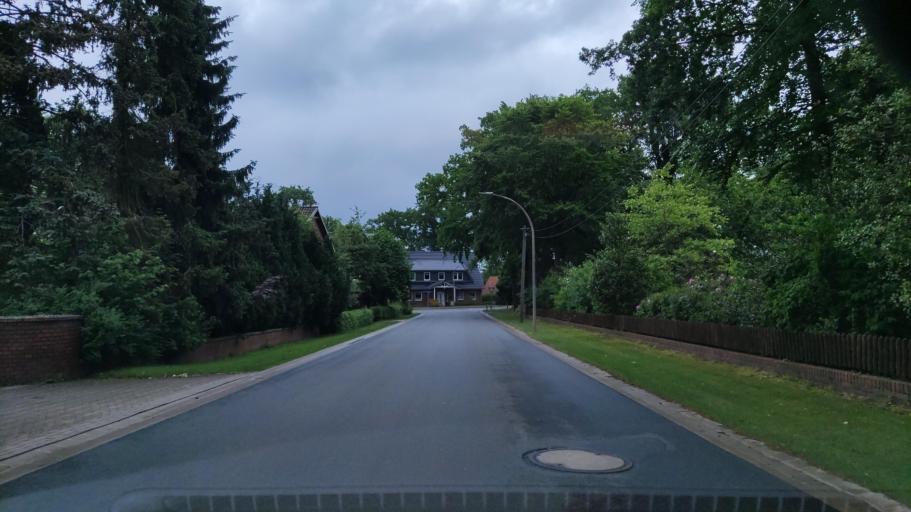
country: DE
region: Lower Saxony
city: Fintel
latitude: 53.0986
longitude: 9.6732
